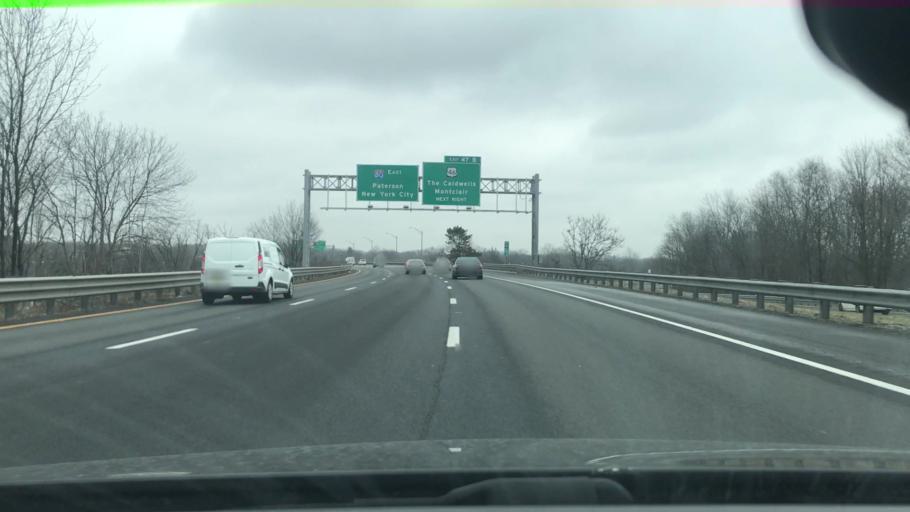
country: US
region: New Jersey
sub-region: Morris County
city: East Hanover
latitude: 40.8587
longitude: -74.3695
